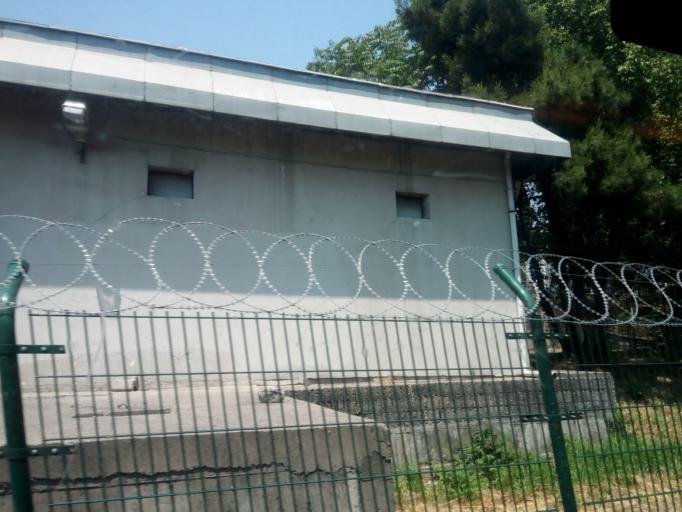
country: TR
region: Istanbul
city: Bahcelievler
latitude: 40.9914
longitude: 28.8398
